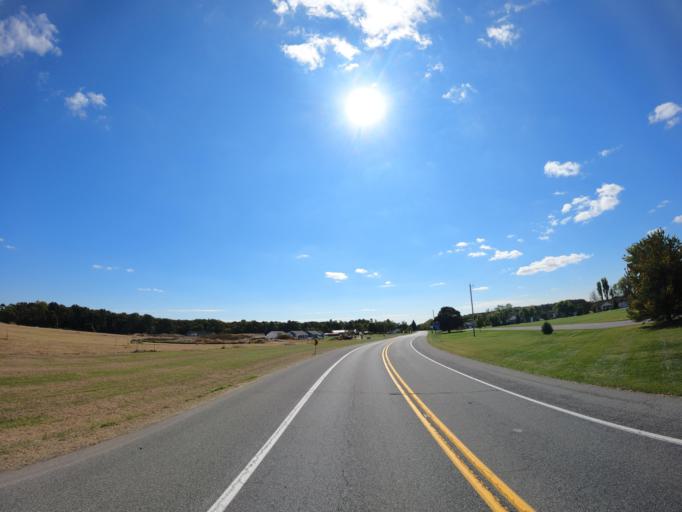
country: US
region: Delaware
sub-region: Sussex County
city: Bridgeville
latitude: 38.8224
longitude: -75.6210
